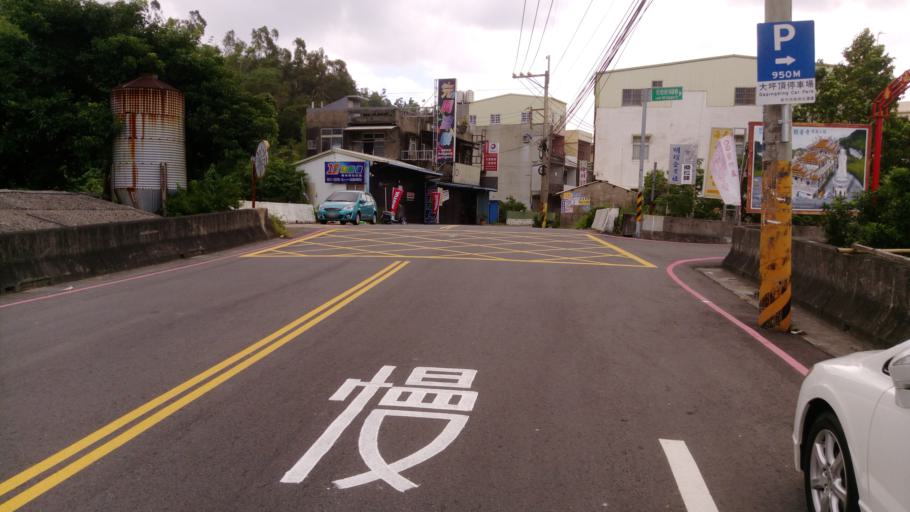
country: TW
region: Taiwan
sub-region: Hsinchu
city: Hsinchu
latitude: 24.7841
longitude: 120.9318
